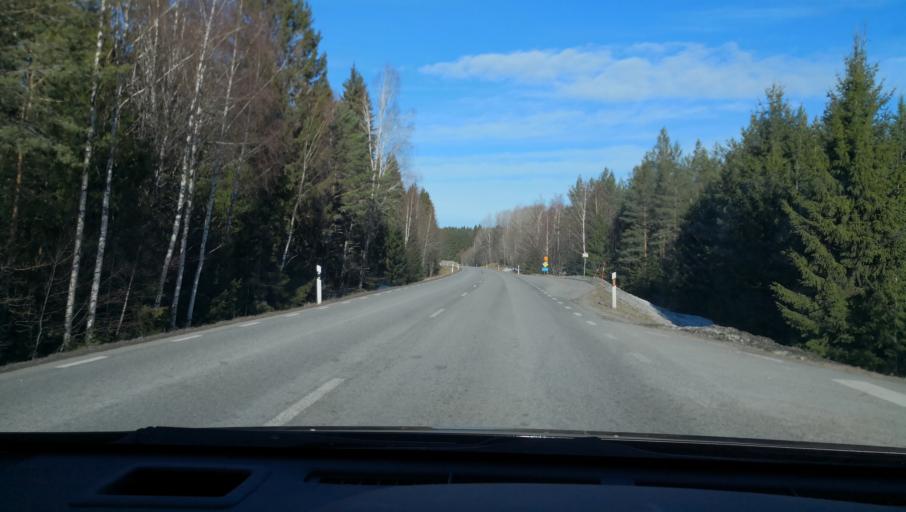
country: SE
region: Uppsala
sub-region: Uppsala Kommun
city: Vattholma
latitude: 60.0247
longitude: 17.7482
